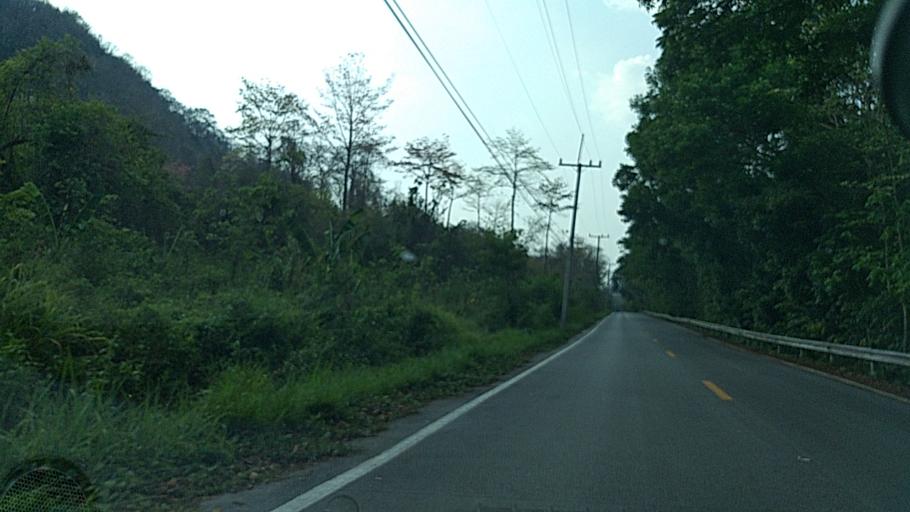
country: TH
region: Sara Buri
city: Saraburi
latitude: 14.4486
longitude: 100.9551
